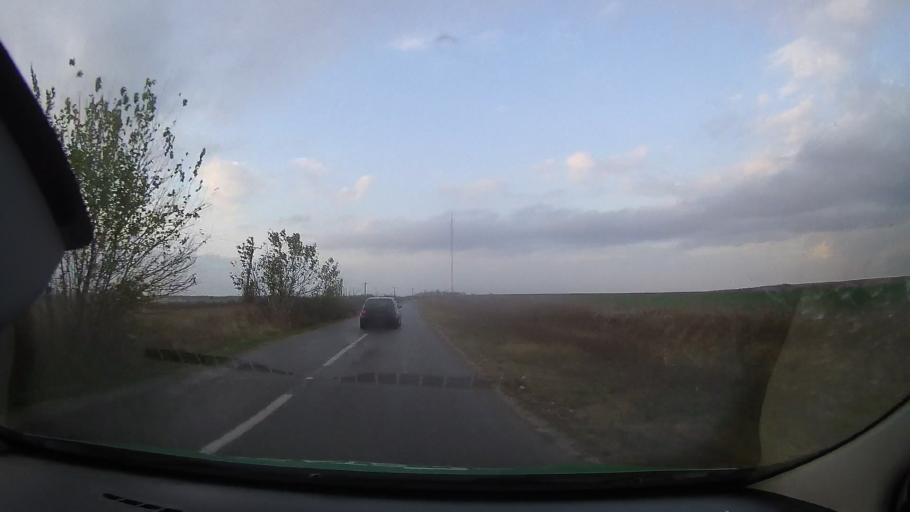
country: RO
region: Constanta
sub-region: Comuna Dobromir
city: Dobromir
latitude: 44.0417
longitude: 27.7562
